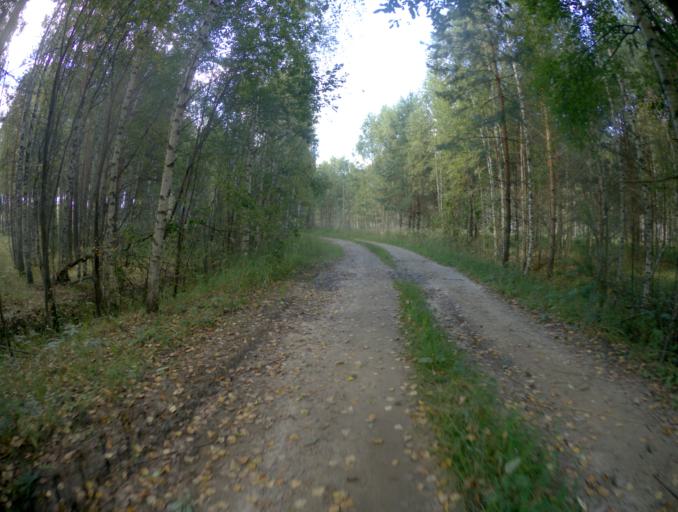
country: RU
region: Vladimir
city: Nikologory
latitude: 56.0146
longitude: 41.8991
